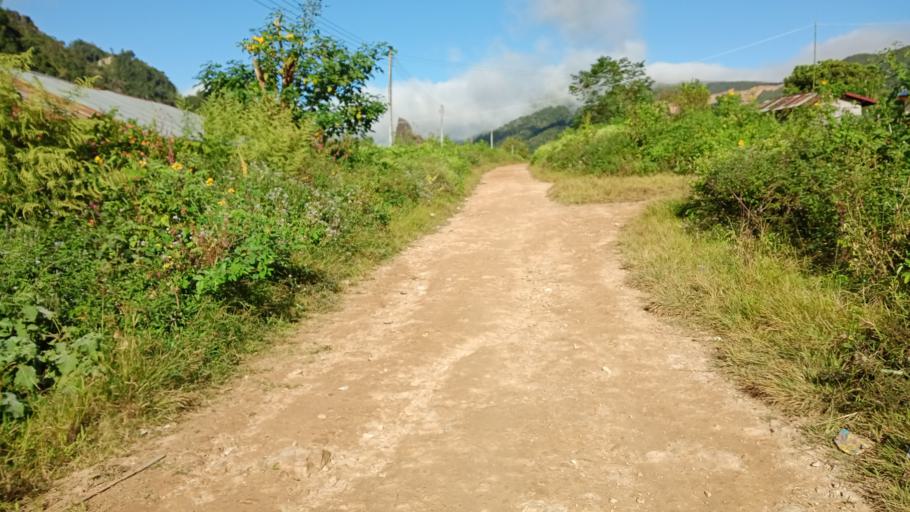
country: LA
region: Xiangkhoang
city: Phonsavan
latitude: 19.1138
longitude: 102.9137
